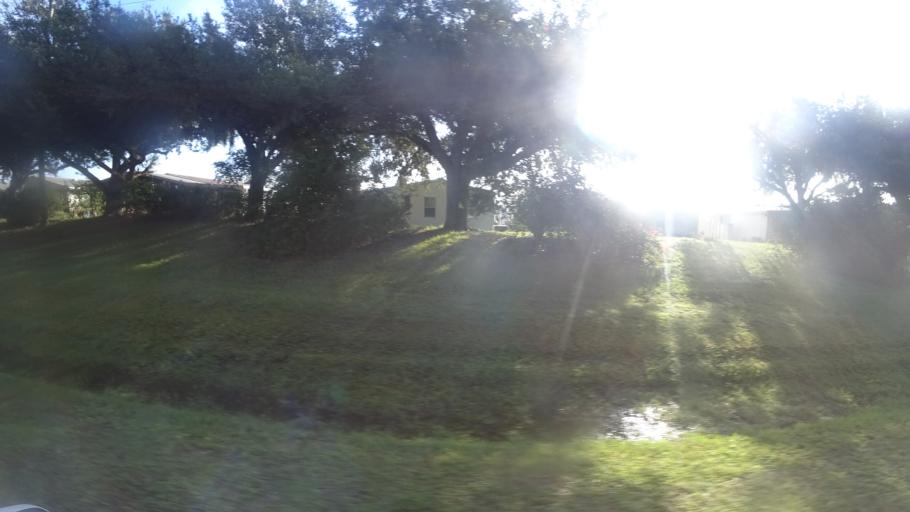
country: US
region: Florida
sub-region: Manatee County
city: Ellenton
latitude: 27.5439
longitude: -82.4664
